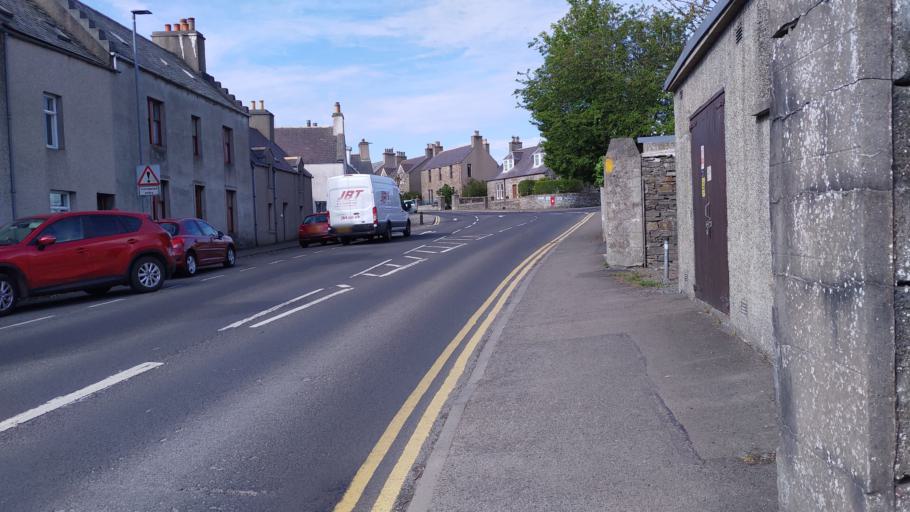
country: GB
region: Scotland
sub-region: Orkney Islands
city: Orkney
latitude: 58.9774
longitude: -2.9668
